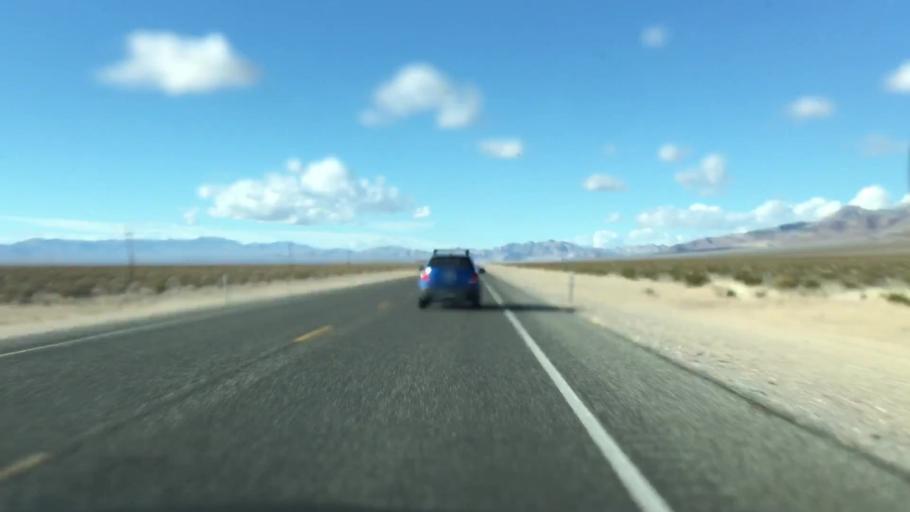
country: US
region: Nevada
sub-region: Nye County
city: Beatty
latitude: 36.7351
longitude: -116.6376
